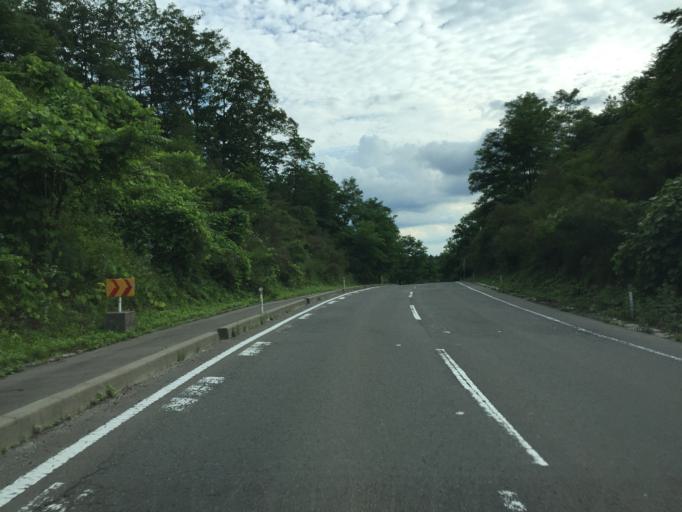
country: JP
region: Fukushima
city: Fukushima-shi
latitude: 37.6974
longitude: 140.5070
